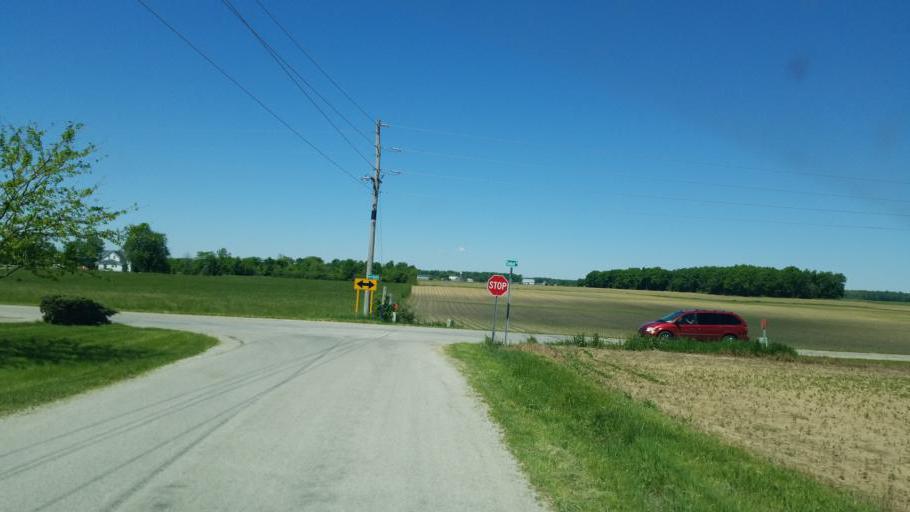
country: US
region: Ohio
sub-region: Shelby County
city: Fort Loramie
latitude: 40.3722
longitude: -84.2780
